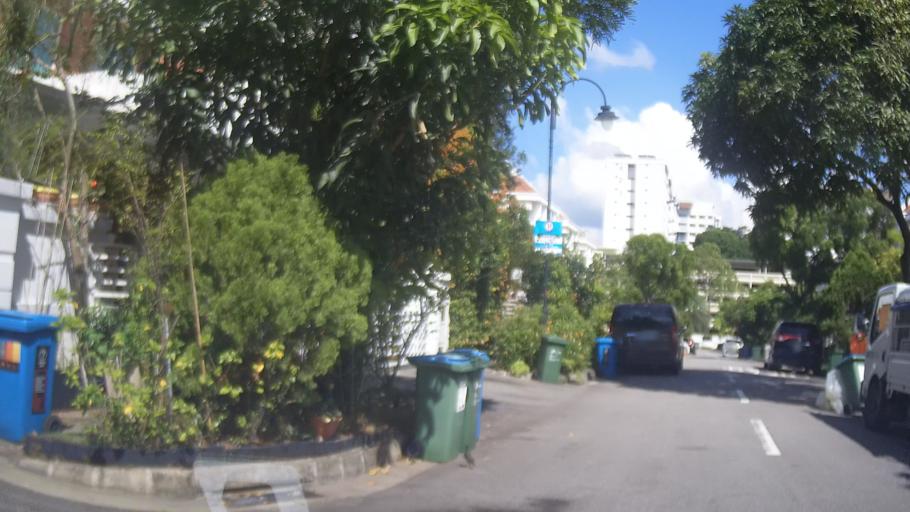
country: MY
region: Johor
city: Johor Bahru
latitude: 1.4279
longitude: 103.7765
